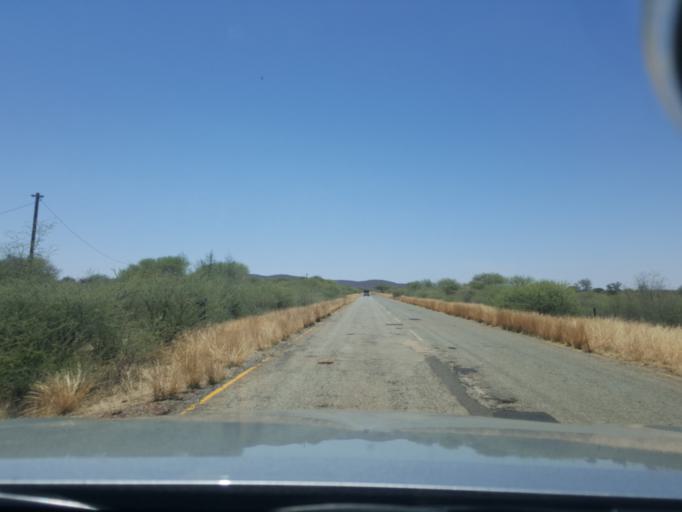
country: BW
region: South East
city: Ramotswa
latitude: -25.0872
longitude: 25.9573
